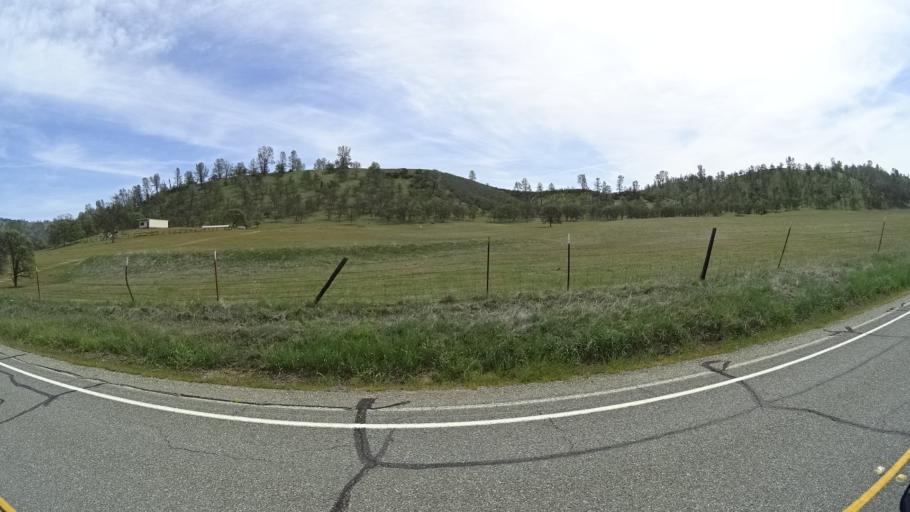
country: US
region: California
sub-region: Glenn County
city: Willows
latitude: 39.5838
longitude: -122.5383
